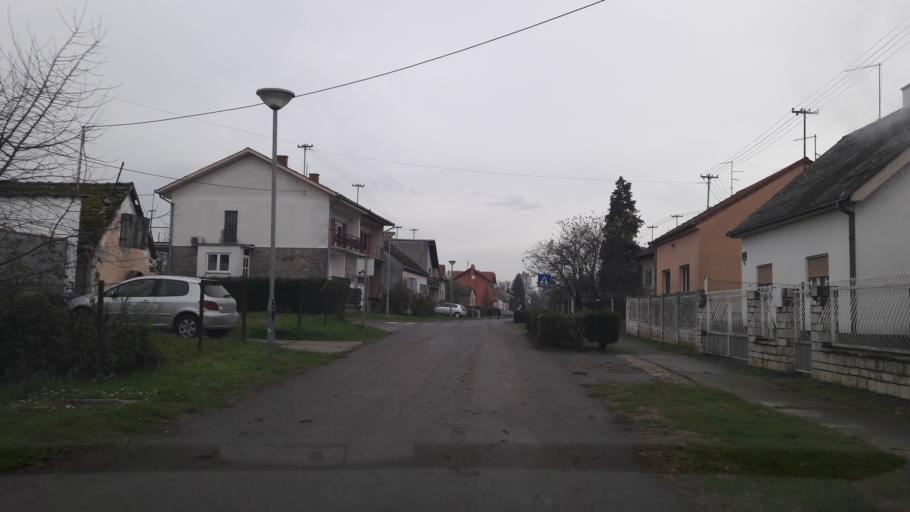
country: HR
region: Osjecko-Baranjska
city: Visnjevac
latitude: 45.5731
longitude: 18.6144
